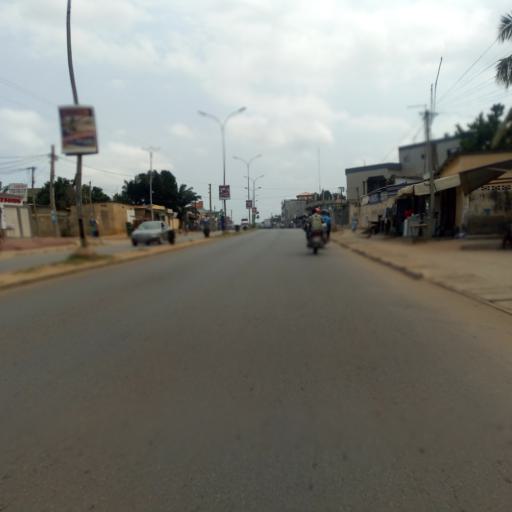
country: TG
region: Maritime
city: Lome
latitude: 6.1935
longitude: 1.1728
